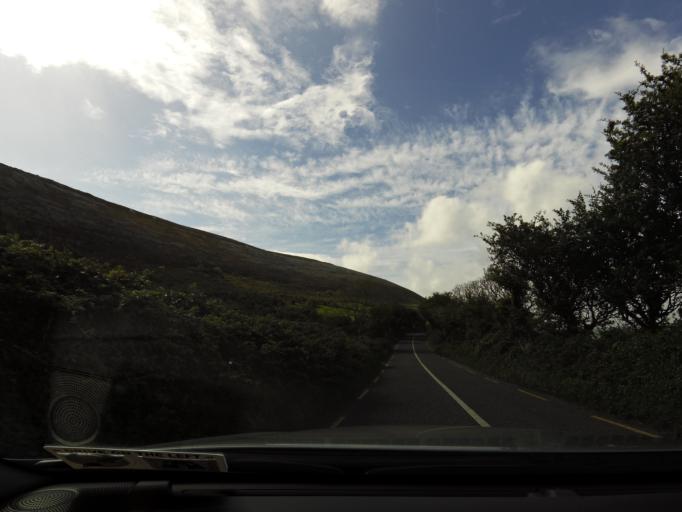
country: IE
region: Connaught
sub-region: County Galway
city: Bearna
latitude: 53.1408
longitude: -9.2278
